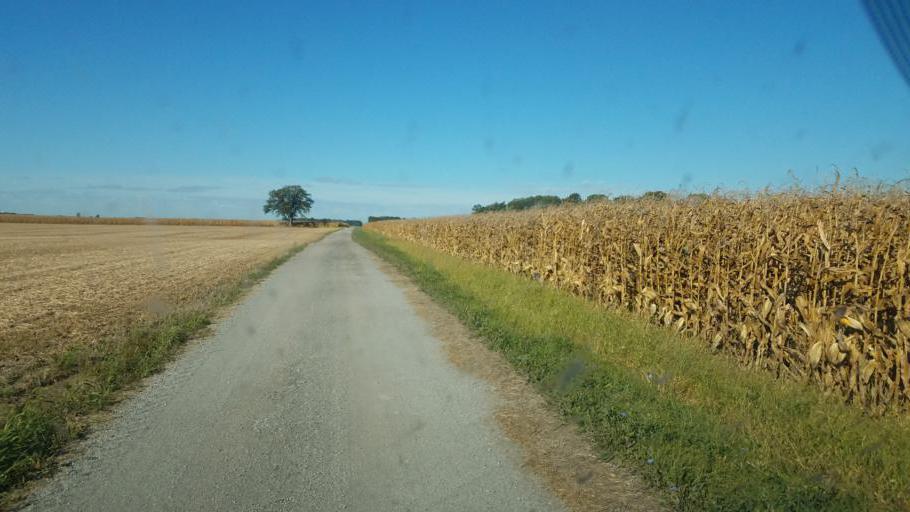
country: US
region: Ohio
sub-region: Marion County
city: Marion
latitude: 40.7023
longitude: -83.1747
